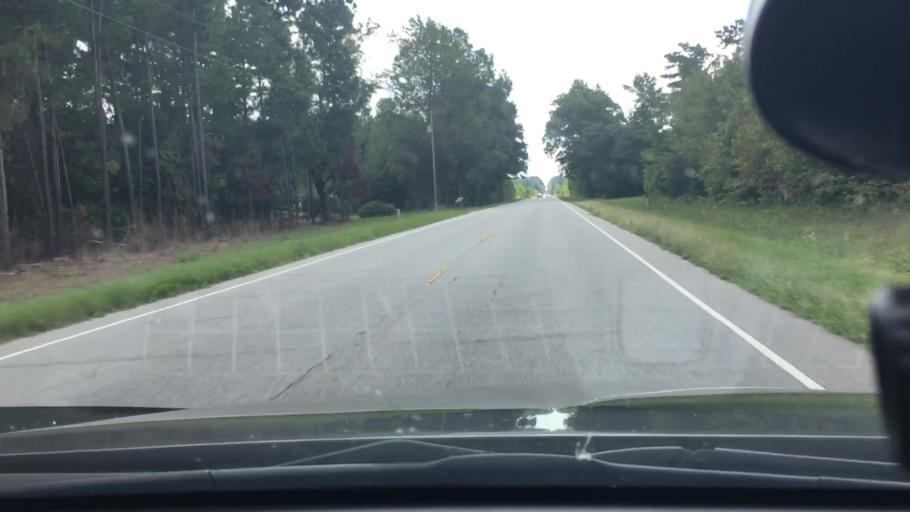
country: US
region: North Carolina
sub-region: Edgecombe County
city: Pinetops
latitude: 35.7760
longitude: -77.5783
